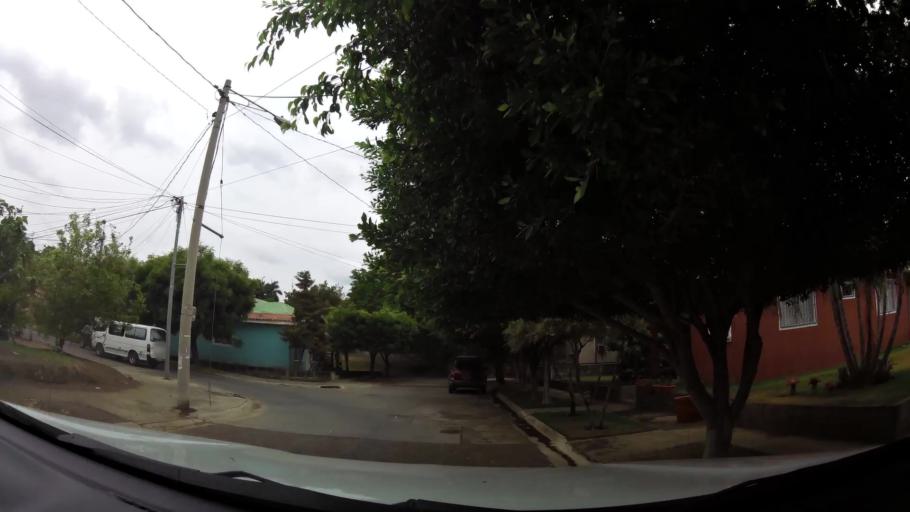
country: NI
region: Masaya
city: Ticuantepe
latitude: 12.0718
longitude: -86.1785
